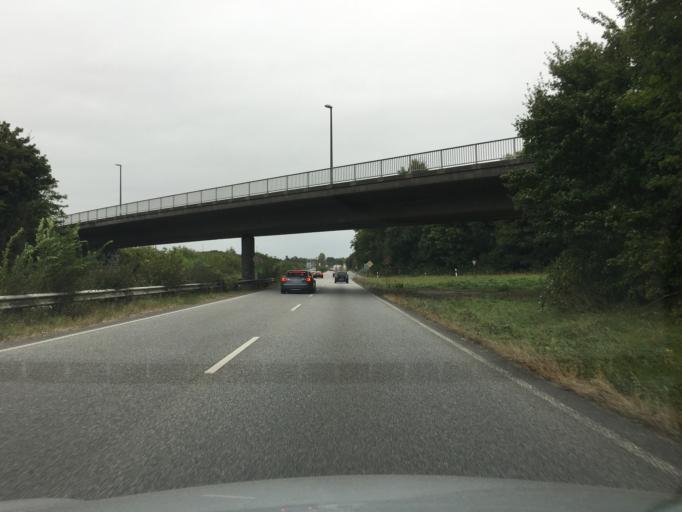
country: DE
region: Schleswig-Holstein
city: Altenholz
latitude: 54.3746
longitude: 10.1292
